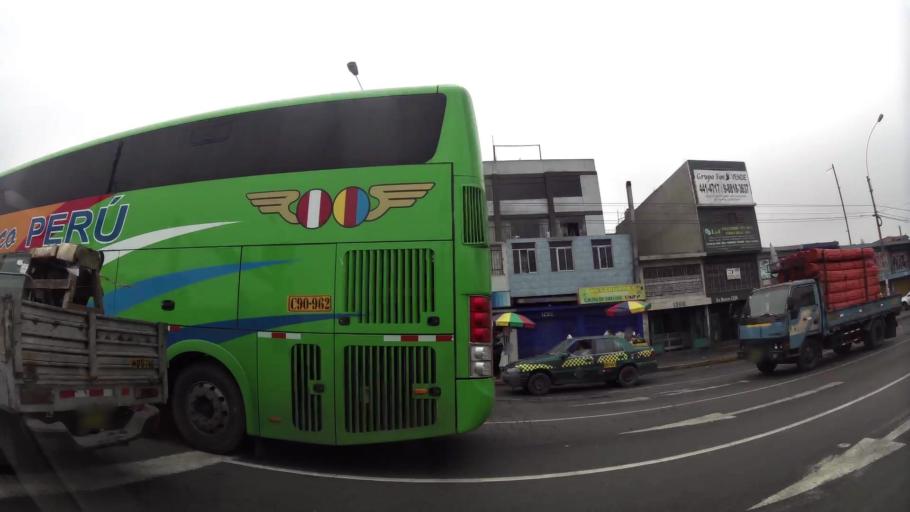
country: PE
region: Lima
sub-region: Lima
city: San Luis
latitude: -12.0734
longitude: -77.0166
